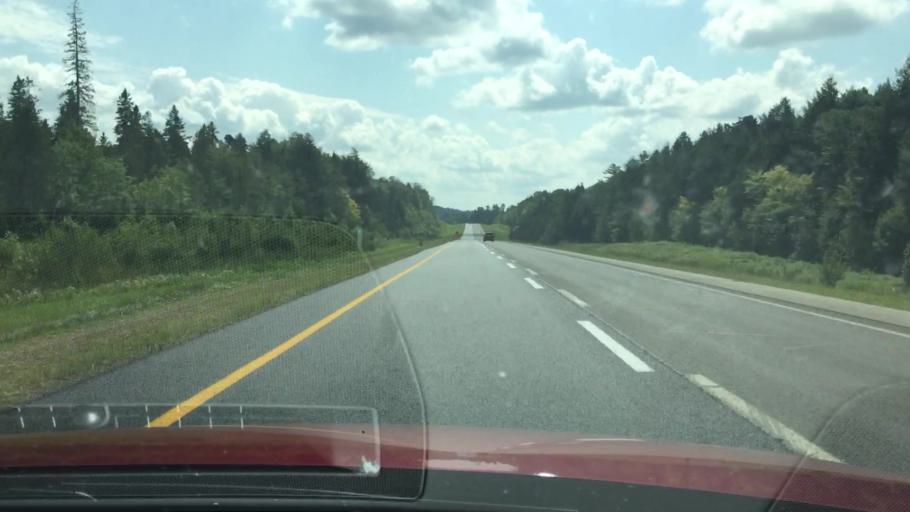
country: US
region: Maine
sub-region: Penobscot County
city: Medway
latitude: 45.7279
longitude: -68.4733
